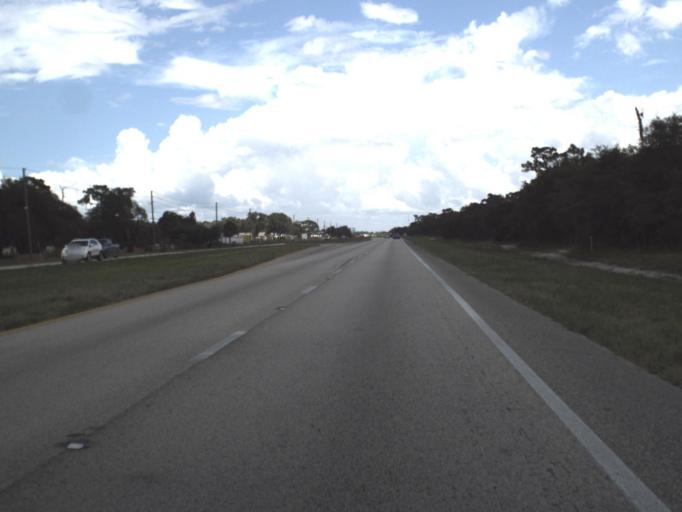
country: US
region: Florida
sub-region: Polk County
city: Lake Wales
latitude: 27.8940
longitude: -81.5277
